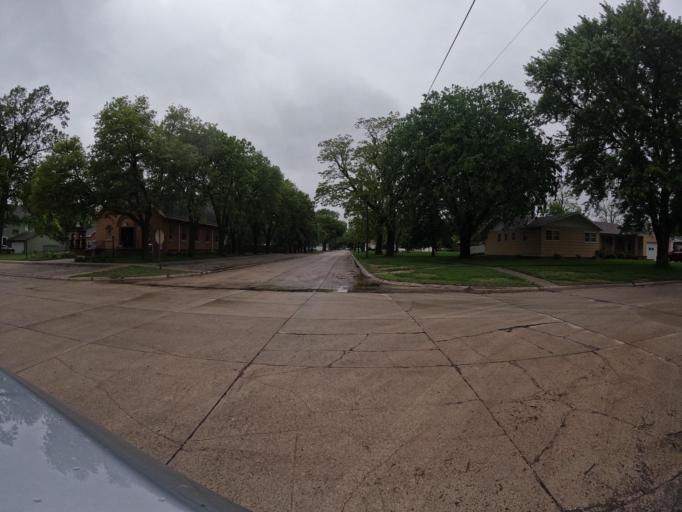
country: US
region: Nebraska
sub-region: Clay County
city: Harvard
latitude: 40.6226
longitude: -98.0943
